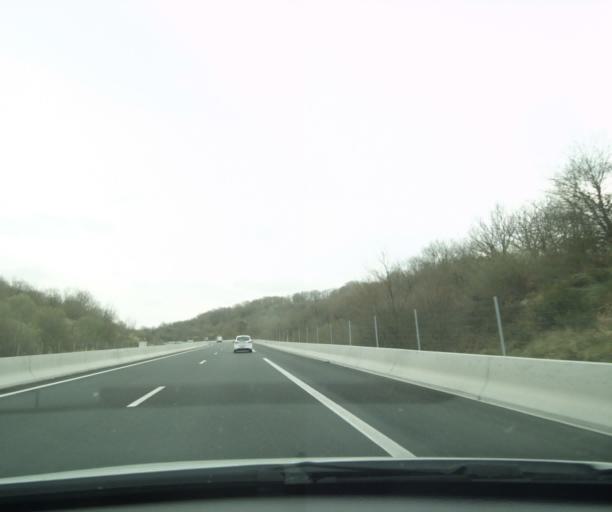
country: FR
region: Aquitaine
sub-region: Departement des Pyrenees-Atlantiques
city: Mouguerre
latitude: 43.4601
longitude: -1.4210
